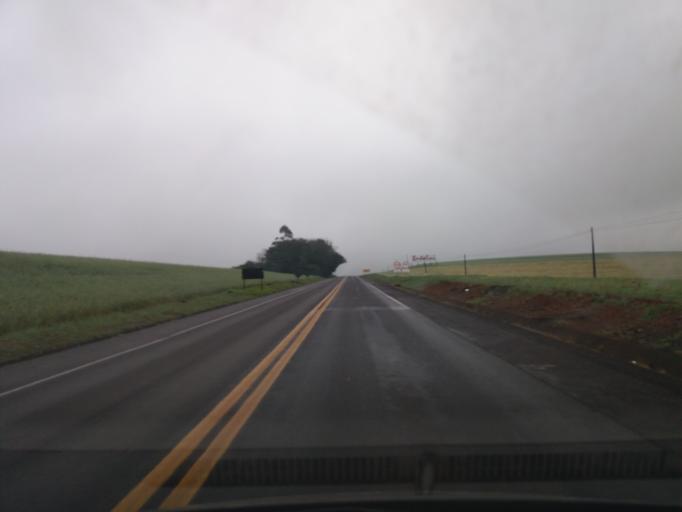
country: BR
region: Parana
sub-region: Ampere
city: Ampere
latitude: -25.8978
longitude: -53.4532
